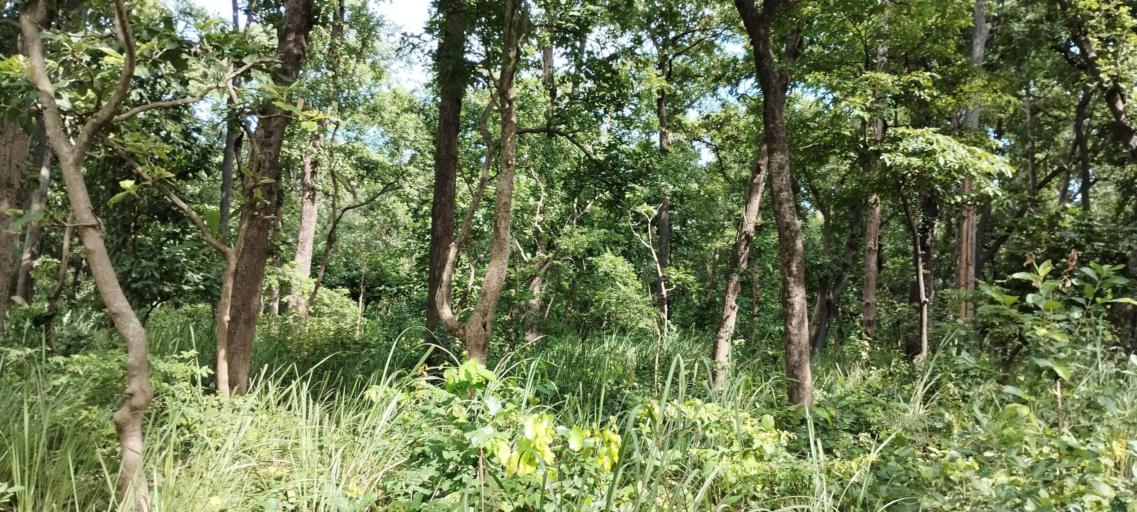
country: NP
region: Far Western
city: Tikapur
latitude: 28.5306
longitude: 81.2833
